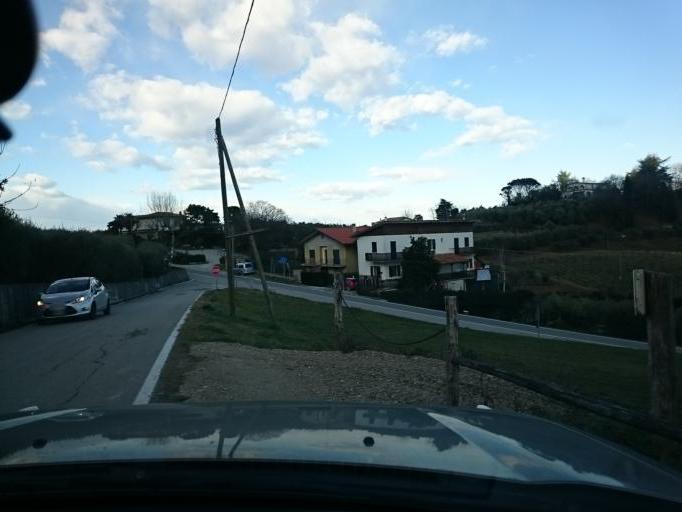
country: IT
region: Veneto
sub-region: Provincia di Padova
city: Treponti
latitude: 45.3677
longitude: 11.6807
